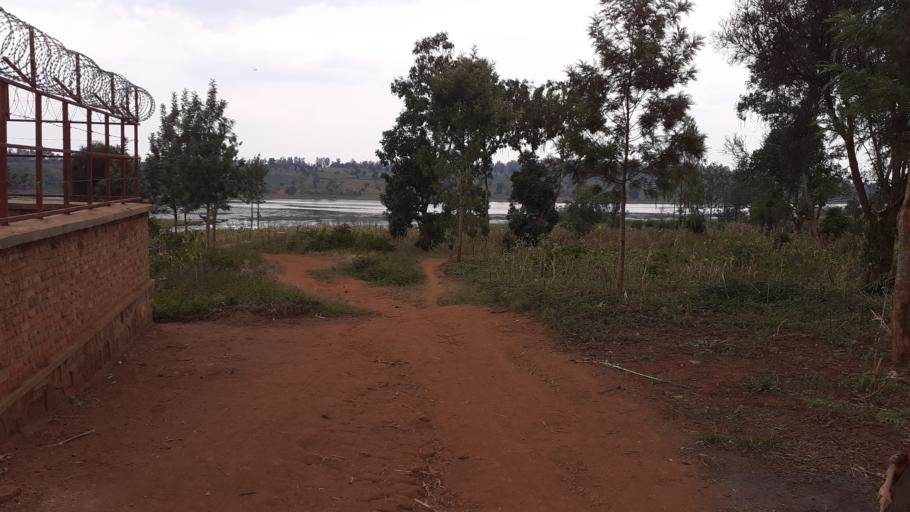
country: BI
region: Kirundo
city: Kirundo
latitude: -2.4534
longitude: 30.1712
